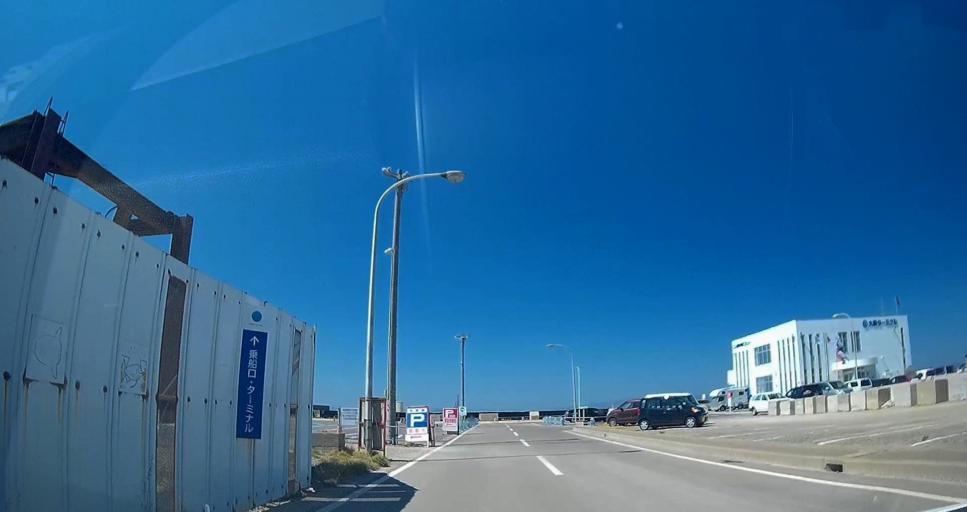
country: JP
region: Hokkaido
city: Hakodate
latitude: 41.5254
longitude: 140.8988
